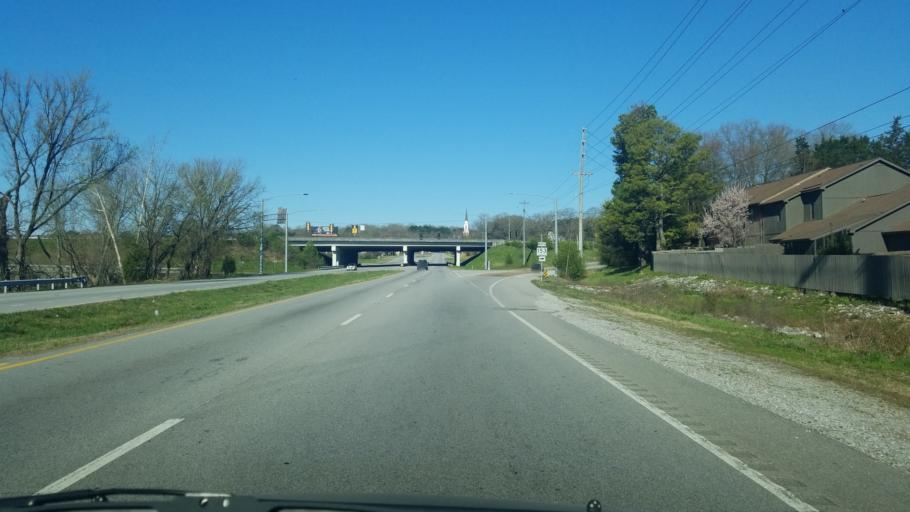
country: US
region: Tennessee
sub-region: Hamilton County
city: East Chattanooga
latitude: 35.0748
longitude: -85.1967
